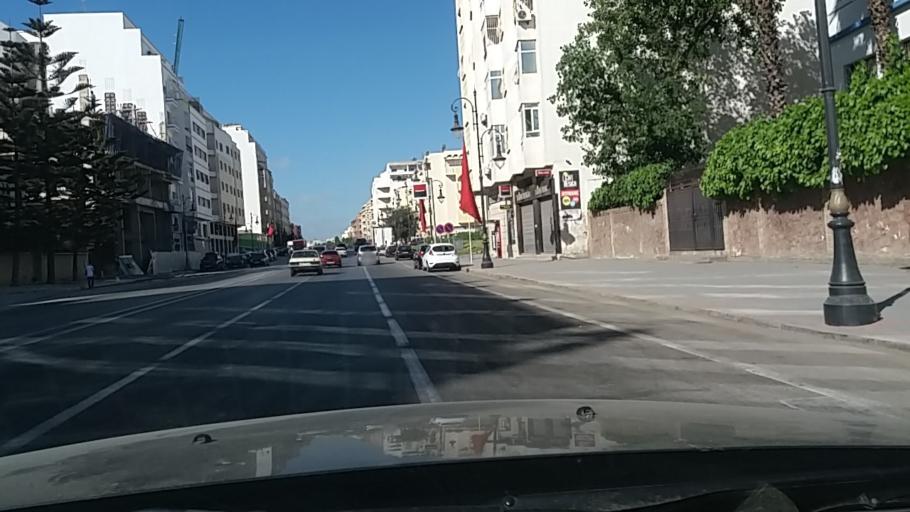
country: MA
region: Tanger-Tetouan
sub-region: Tanger-Assilah
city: Tangier
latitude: 35.7649
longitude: -5.8360
